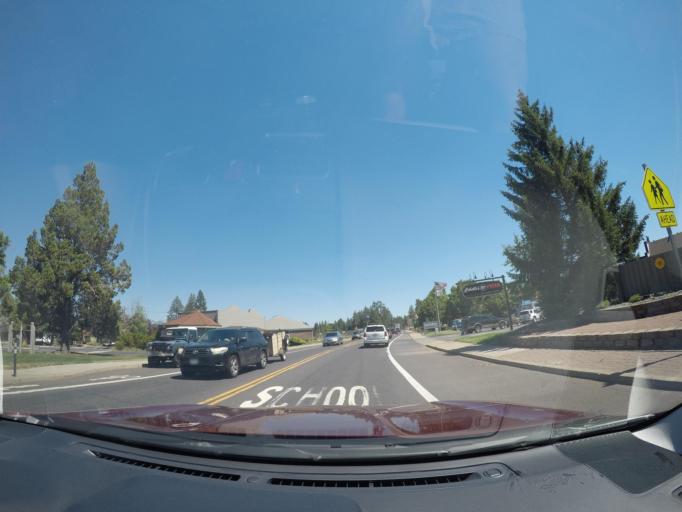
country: US
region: Oregon
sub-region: Deschutes County
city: Sisters
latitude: 44.2912
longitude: -121.5458
